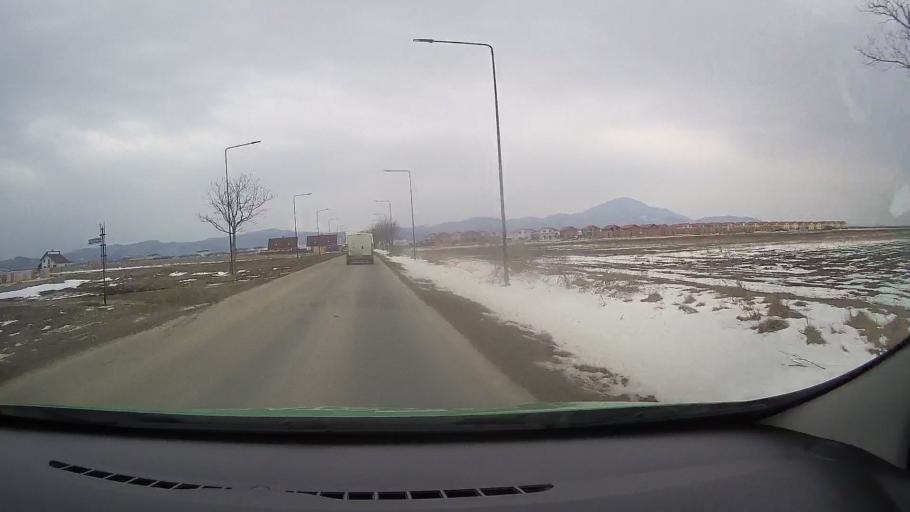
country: RO
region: Brasov
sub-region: Comuna Cristian
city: Cristian
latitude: 45.6283
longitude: 25.4686
